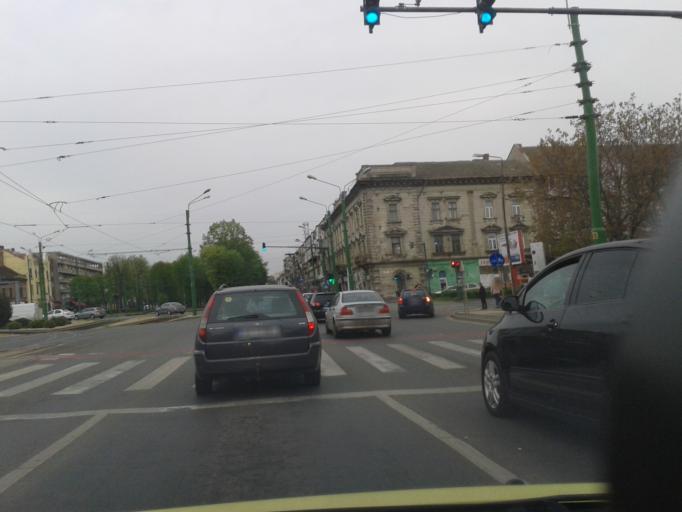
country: RO
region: Arad
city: Arad
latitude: 46.1834
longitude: 21.3238
